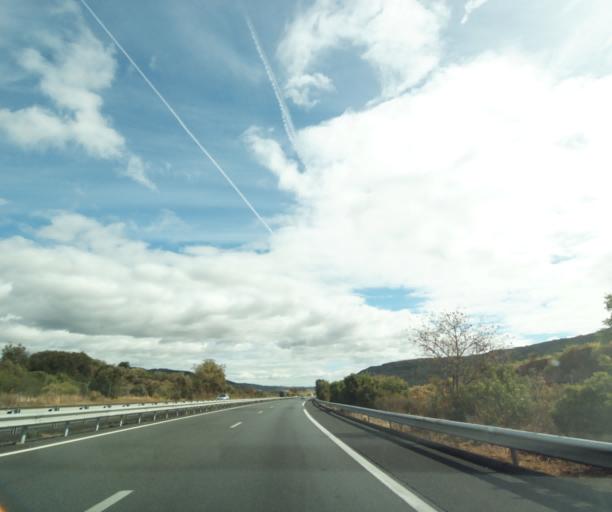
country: FR
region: Languedoc-Roussillon
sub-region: Departement de l'Herault
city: Lodeve
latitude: 43.6849
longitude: 3.3669
